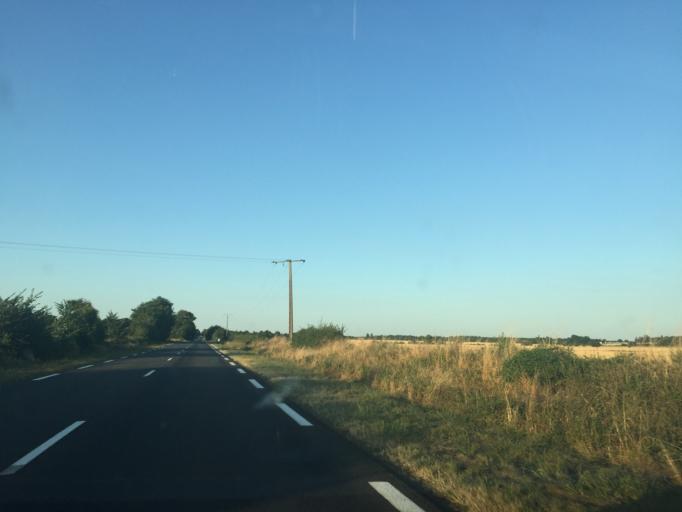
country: FR
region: Poitou-Charentes
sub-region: Departement de la Vienne
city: Rouille
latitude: 46.3933
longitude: 0.0604
